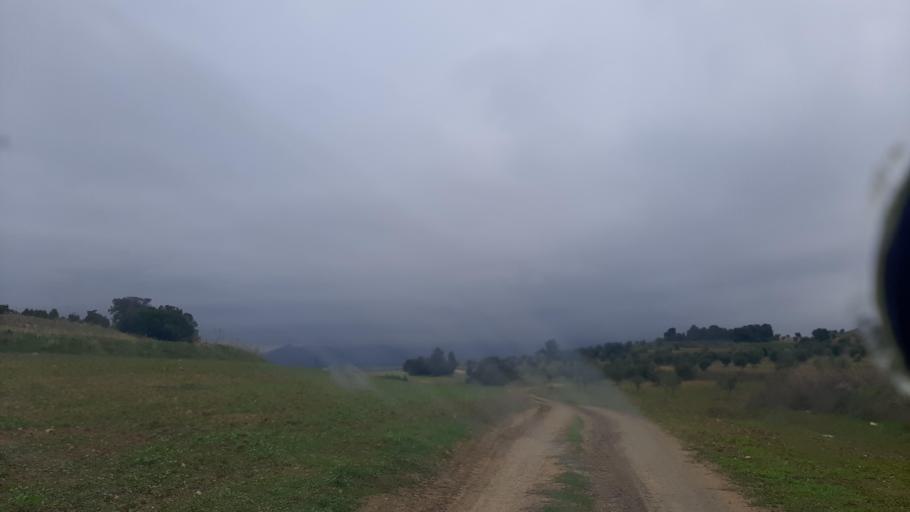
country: TN
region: Tunis
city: La Sebala du Mornag
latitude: 36.5770
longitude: 10.2913
